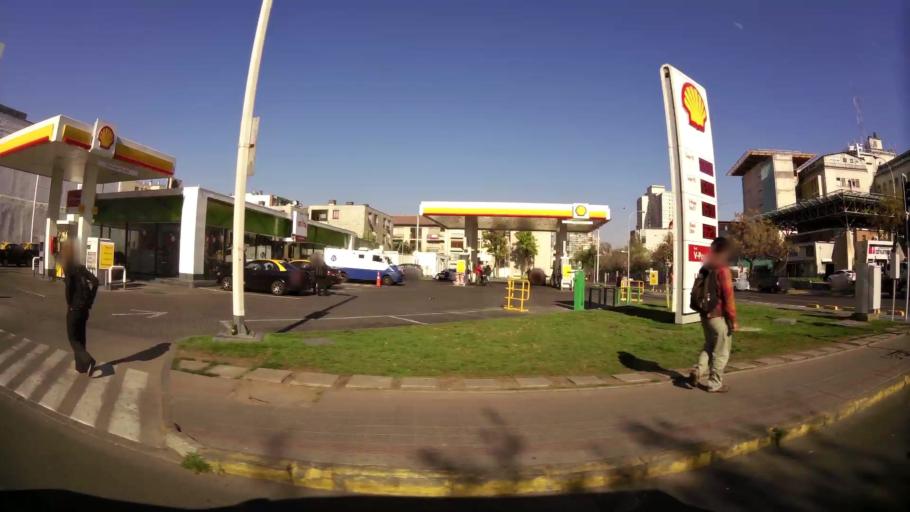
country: CL
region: Santiago Metropolitan
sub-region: Provincia de Santiago
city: Santiago
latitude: -33.4447
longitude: -70.6369
